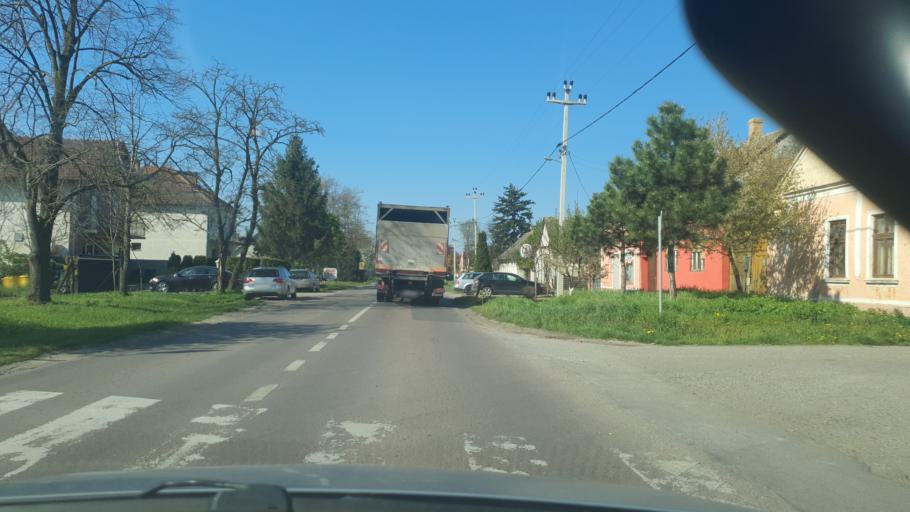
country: RS
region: Autonomna Pokrajina Vojvodina
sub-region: Zapadnobacki Okrug
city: Sombor
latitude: 45.7723
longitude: 19.2722
